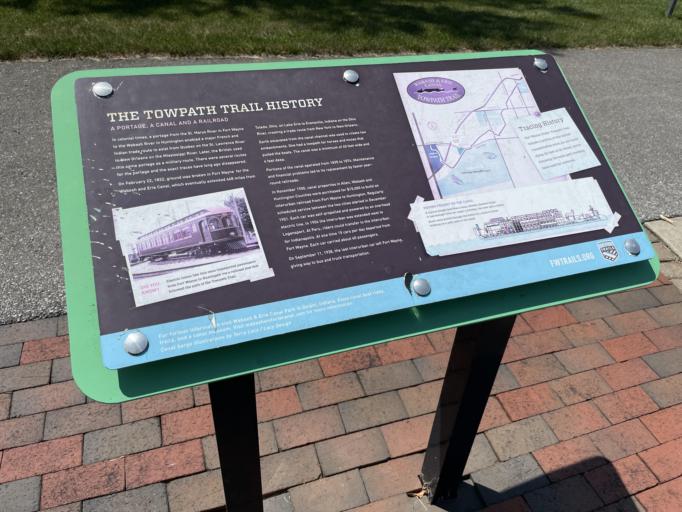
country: US
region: Indiana
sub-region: Allen County
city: Fort Wayne
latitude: 41.0423
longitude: -85.2312
